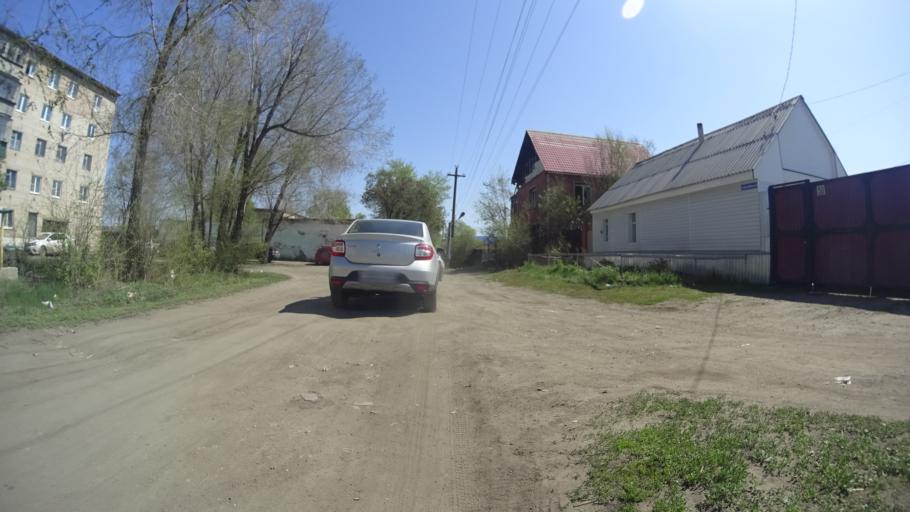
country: RU
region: Chelyabinsk
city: Troitsk
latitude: 54.0945
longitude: 61.5761
